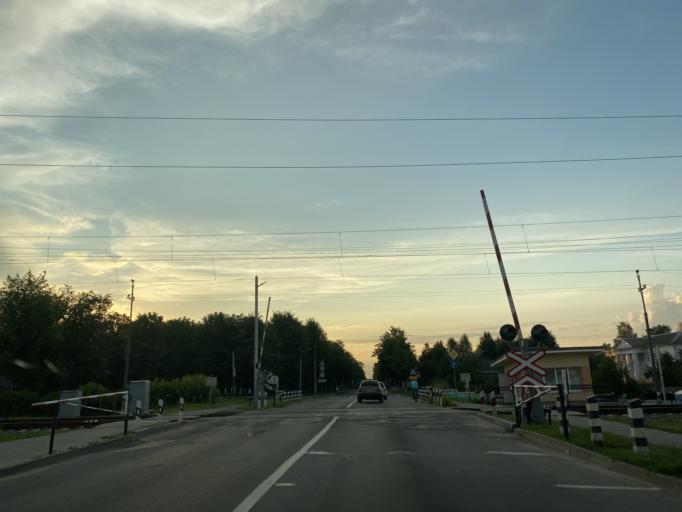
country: BY
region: Brest
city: Ivatsevichy
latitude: 52.7116
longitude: 25.3514
